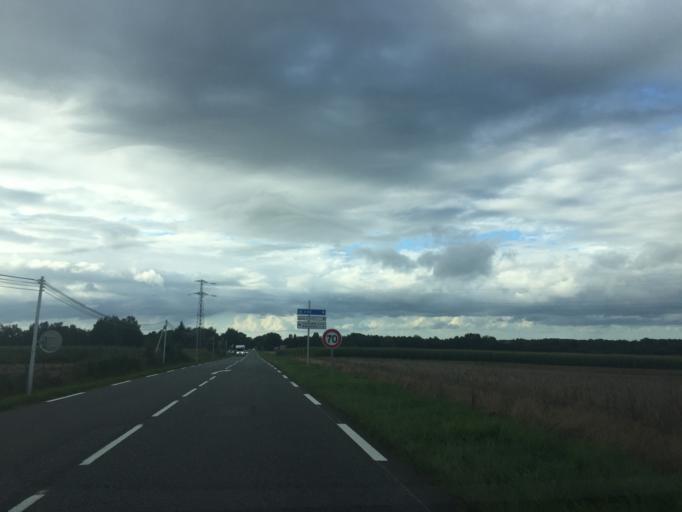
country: FR
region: Midi-Pyrenees
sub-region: Departement des Hautes-Pyrenees
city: Capvern
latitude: 43.0948
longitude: 0.3323
